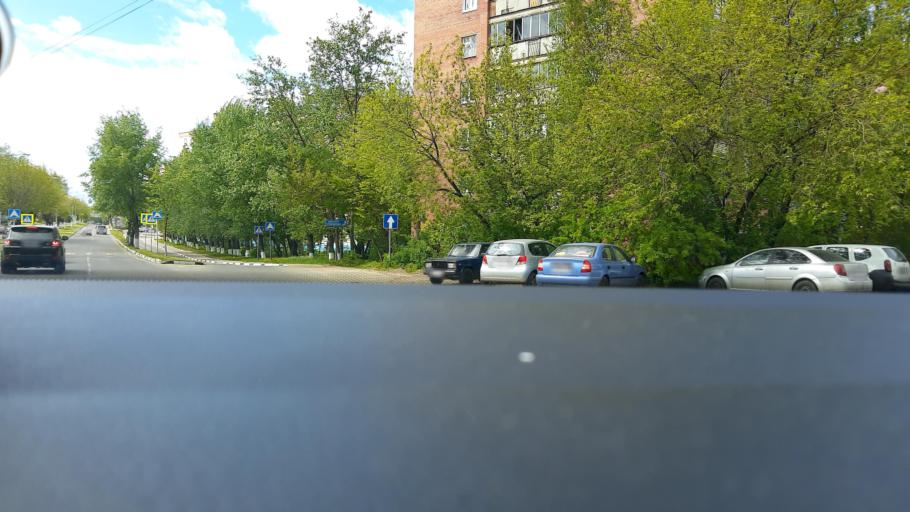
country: RU
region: Moskovskaya
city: Dmitrov
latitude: 56.3490
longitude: 37.5324
